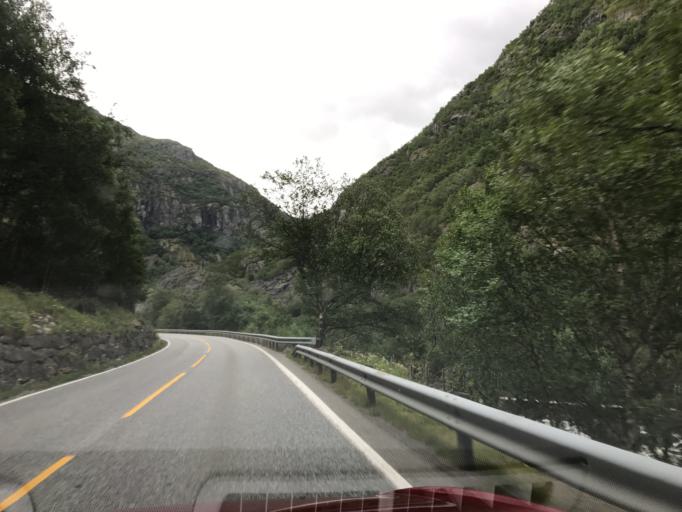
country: NO
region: Hordaland
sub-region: Eidfjord
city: Eidfjord
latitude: 60.4187
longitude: 7.1707
